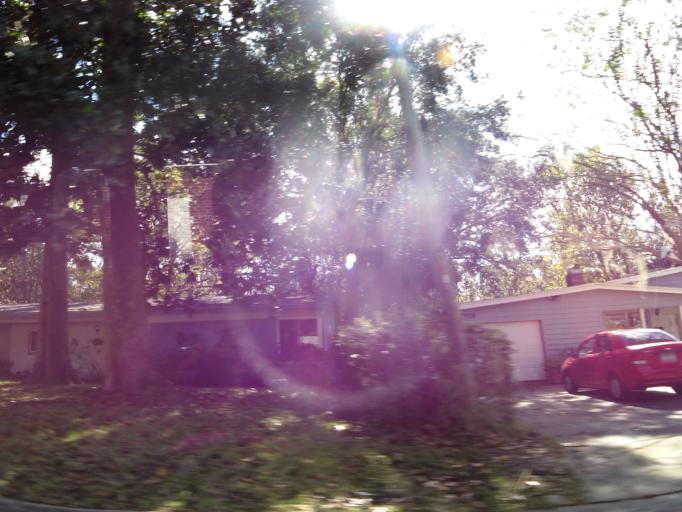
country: US
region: Florida
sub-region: Duval County
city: Jacksonville
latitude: 30.2553
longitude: -81.6376
